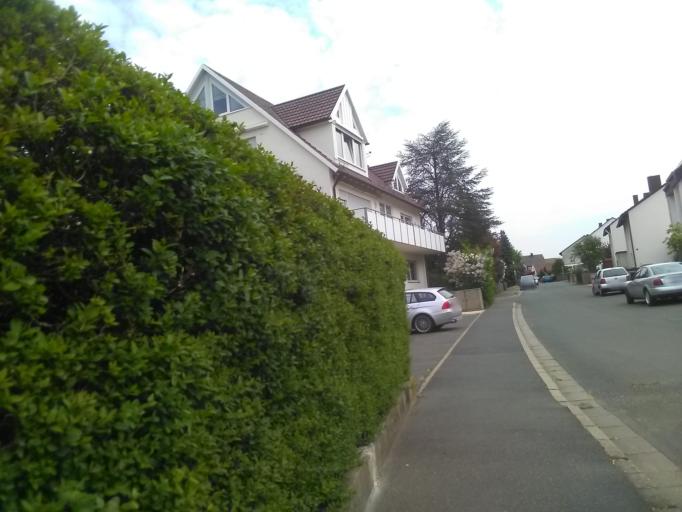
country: DE
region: Bavaria
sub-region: Upper Franconia
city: Kleinsendelbach
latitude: 49.5720
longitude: 11.1999
